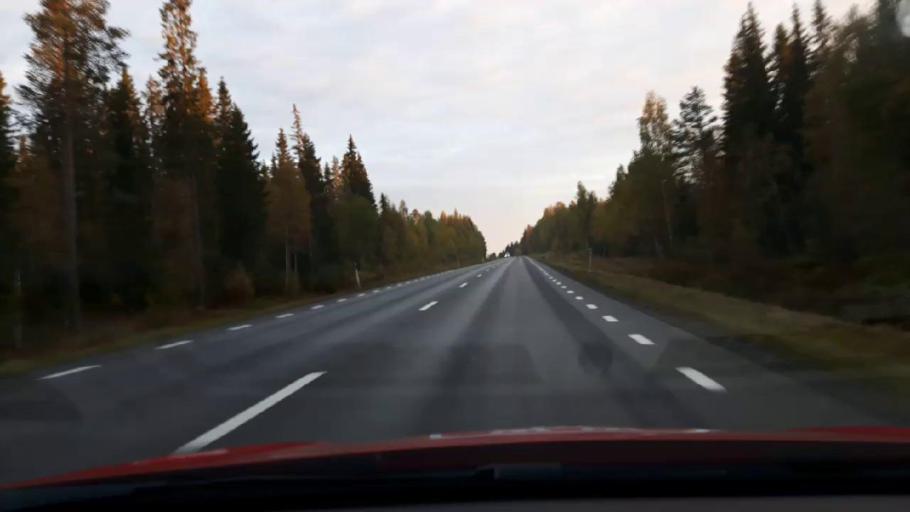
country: SE
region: Jaemtland
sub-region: OEstersunds Kommun
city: Lit
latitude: 63.3052
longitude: 14.8705
